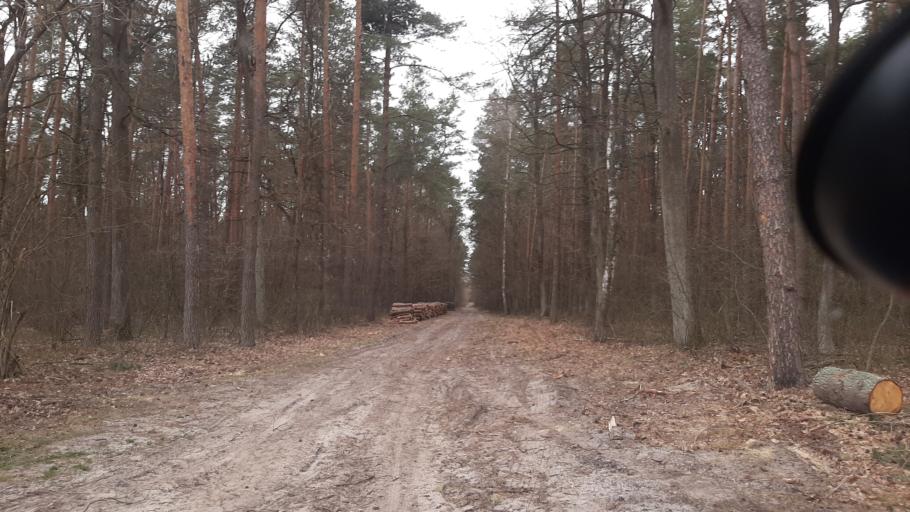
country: PL
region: Lublin Voivodeship
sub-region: Powiat lubelski
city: Garbow
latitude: 51.3988
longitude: 22.3726
